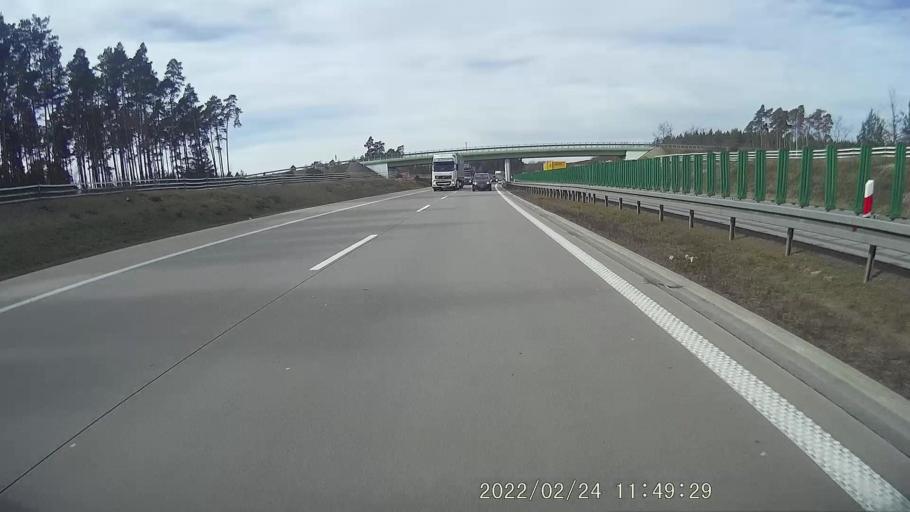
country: PL
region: Lower Silesian Voivodeship
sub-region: Powiat polkowicki
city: Radwanice
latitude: 51.5955
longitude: 15.9598
